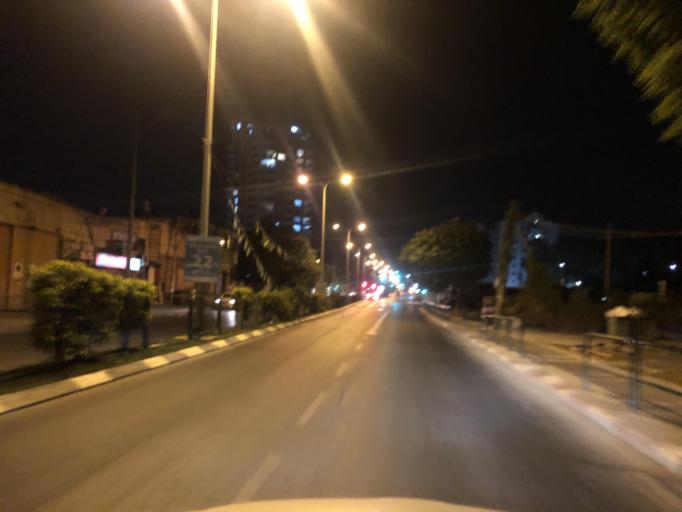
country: IL
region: Tel Aviv
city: Azor
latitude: 32.0472
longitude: 34.7974
